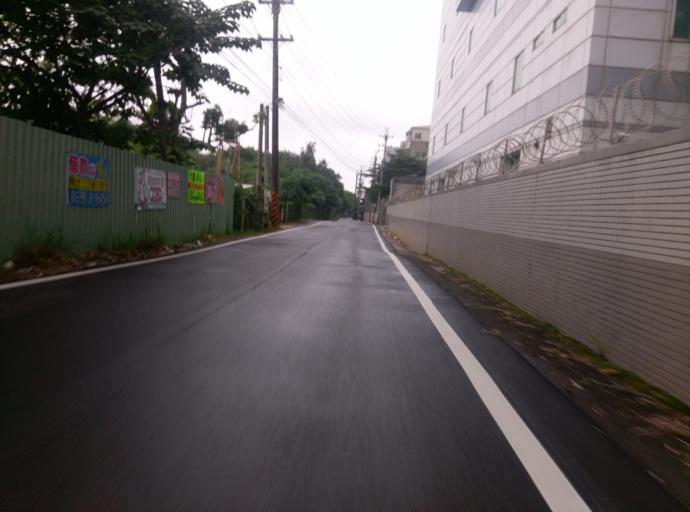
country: TW
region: Taiwan
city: Daxi
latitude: 24.9093
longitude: 121.2408
